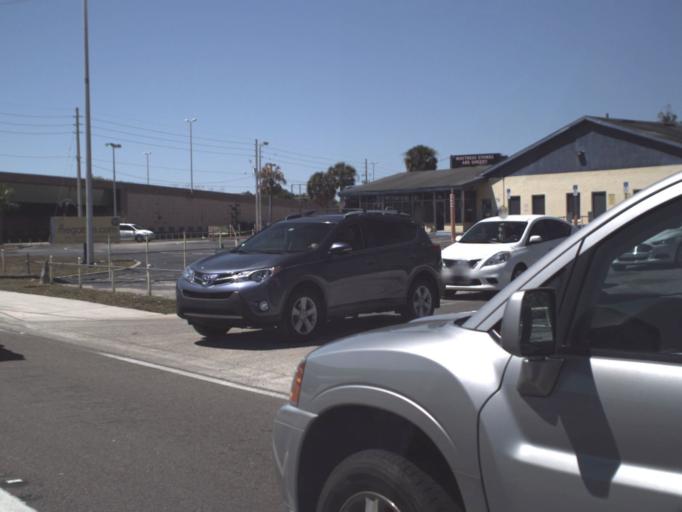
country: US
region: Florida
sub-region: Orange County
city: Azalea Park
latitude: 28.5581
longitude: -81.3109
